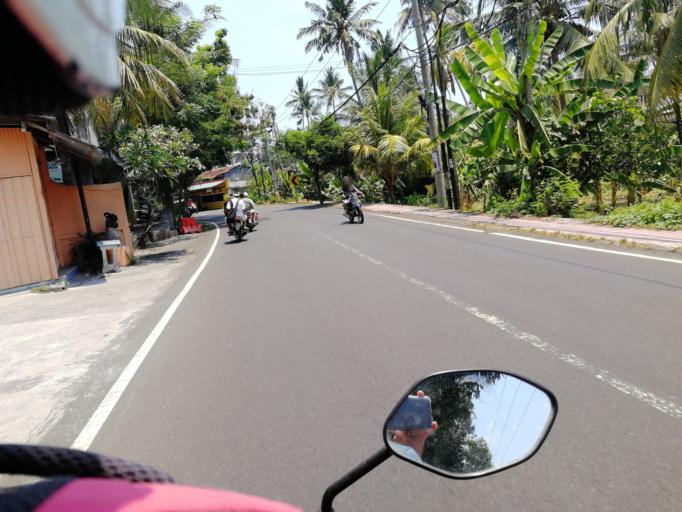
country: ID
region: Bali
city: Banjar Pegeringsingan
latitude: -8.5049
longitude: 115.5594
